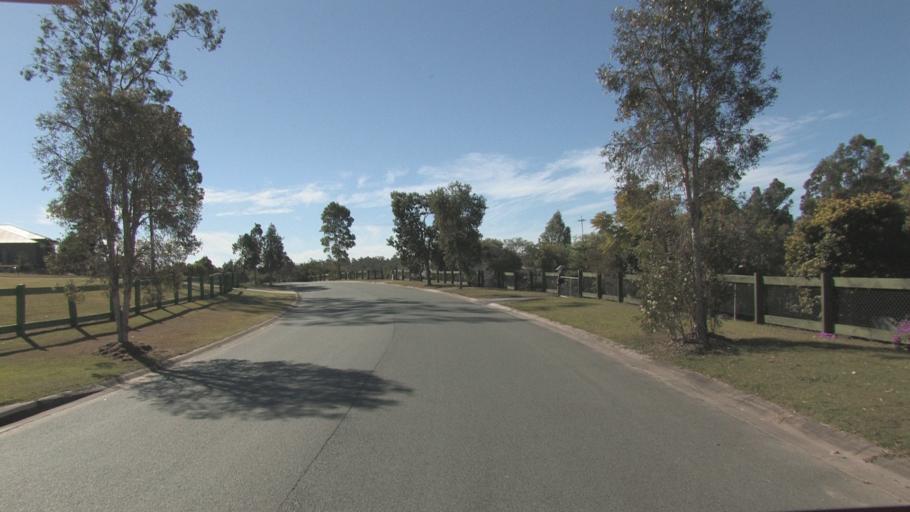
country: AU
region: Queensland
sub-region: Ipswich
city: Springfield Lakes
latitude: -27.7434
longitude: 152.9222
